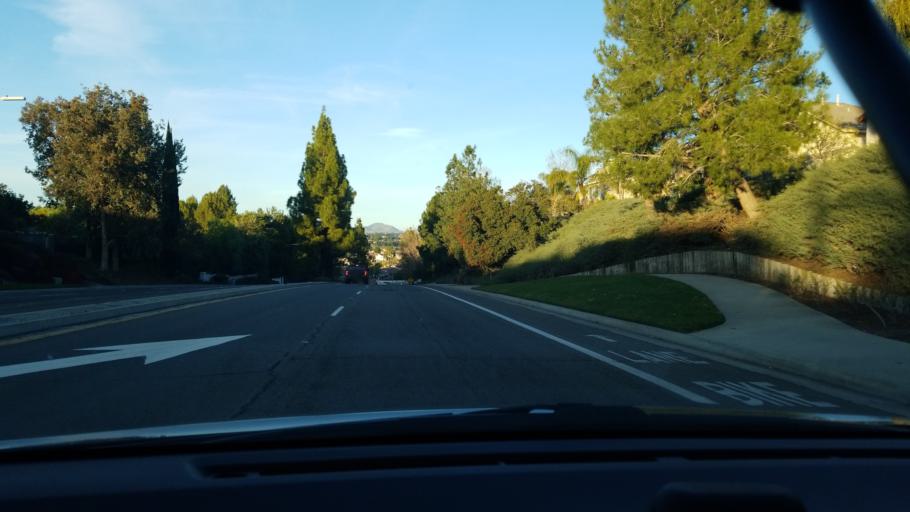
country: US
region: California
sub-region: Riverside County
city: Temecula
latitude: 33.4701
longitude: -117.0951
